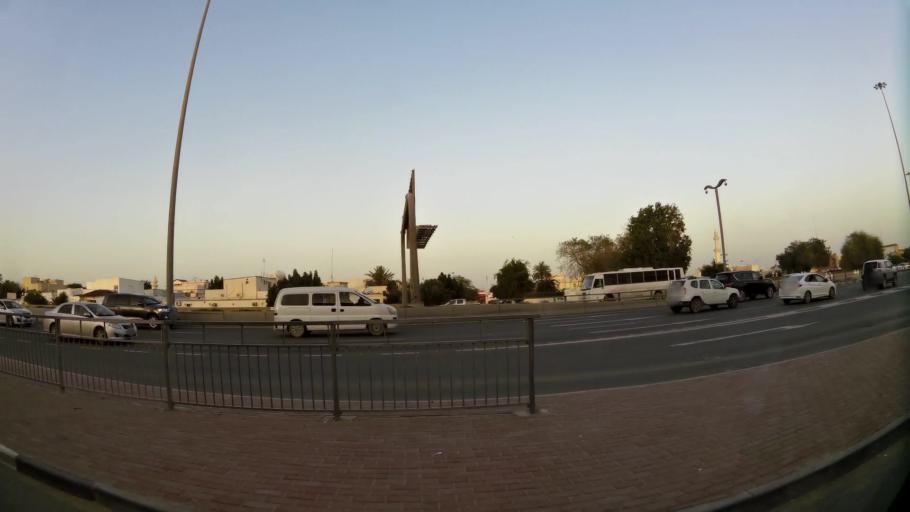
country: QA
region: Baladiyat ar Rayyan
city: Ar Rayyan
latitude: 25.3246
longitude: 51.4678
